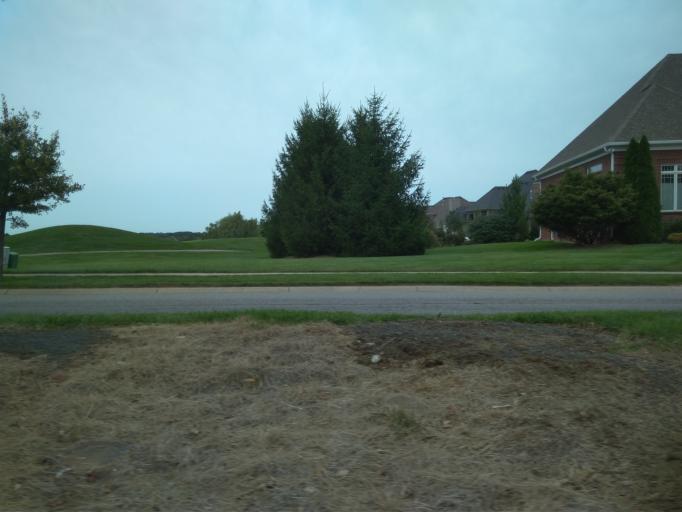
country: US
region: Kentucky
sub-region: Oldham County
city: Pewee Valley
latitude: 38.2748
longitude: -85.4858
